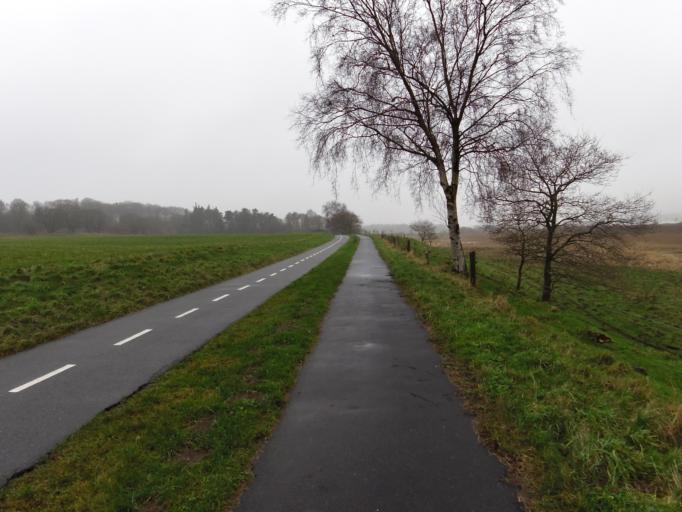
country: DK
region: Central Jutland
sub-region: Arhus Kommune
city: Stavtrup
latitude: 56.1437
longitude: 10.0977
